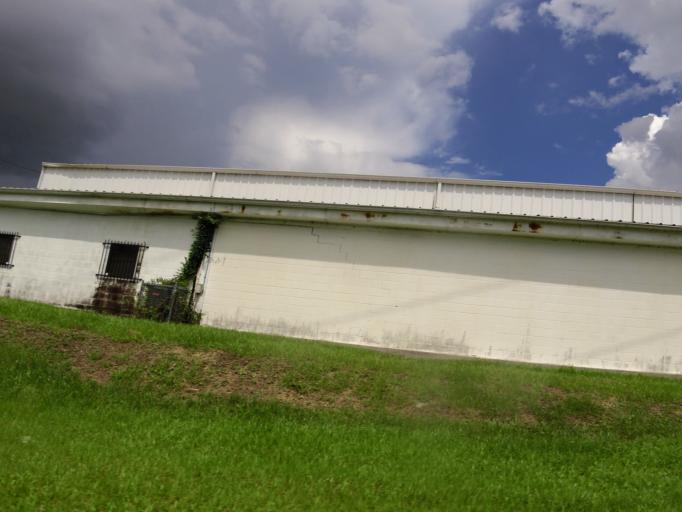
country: US
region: Florida
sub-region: Duval County
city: Jacksonville
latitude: 30.3705
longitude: -81.6392
